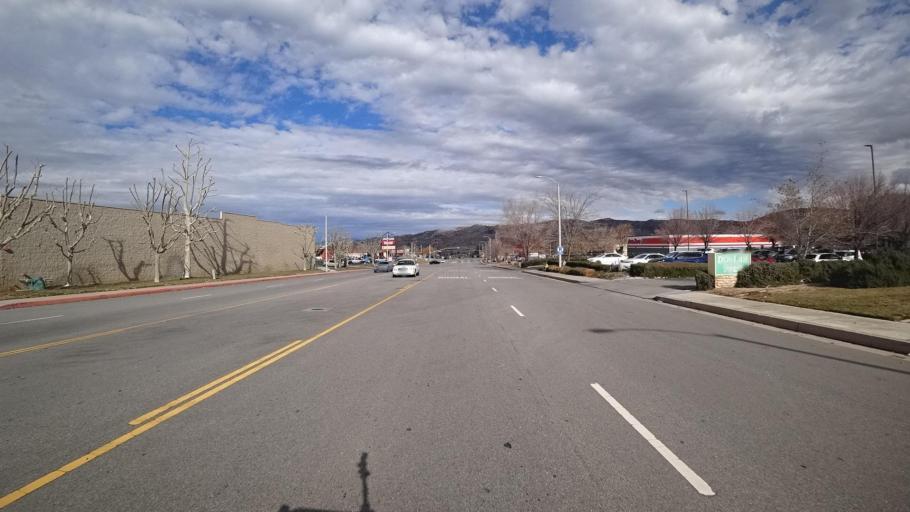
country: US
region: California
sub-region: Kern County
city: Tehachapi
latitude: 35.1222
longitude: -118.4678
